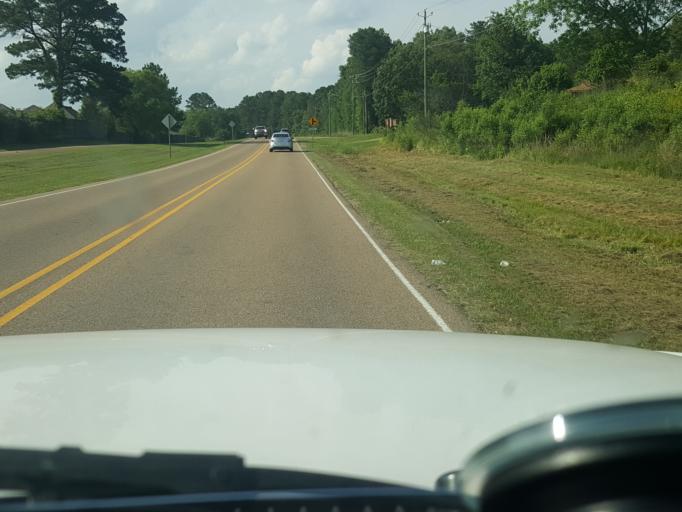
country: US
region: Mississippi
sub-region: Madison County
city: Madison
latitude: 32.4083
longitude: -90.0089
